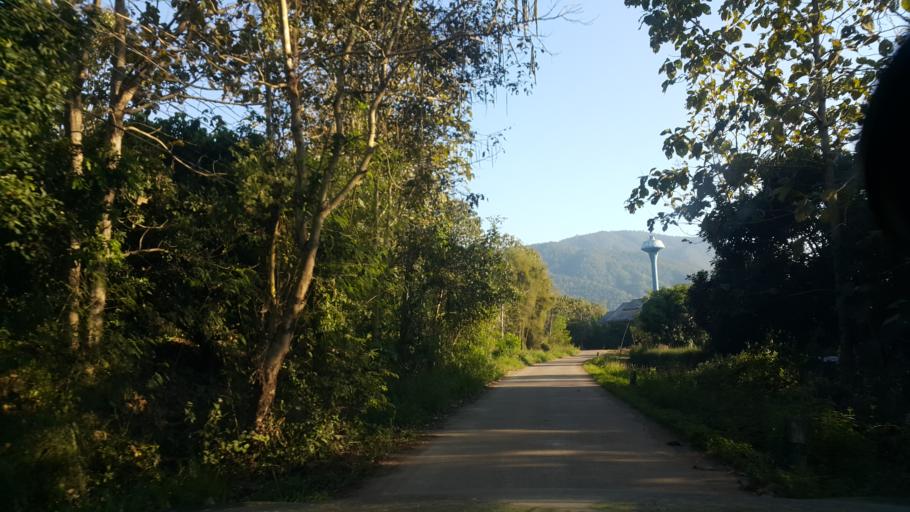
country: TH
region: Chiang Mai
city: Mae On
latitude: 18.7684
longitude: 99.2663
